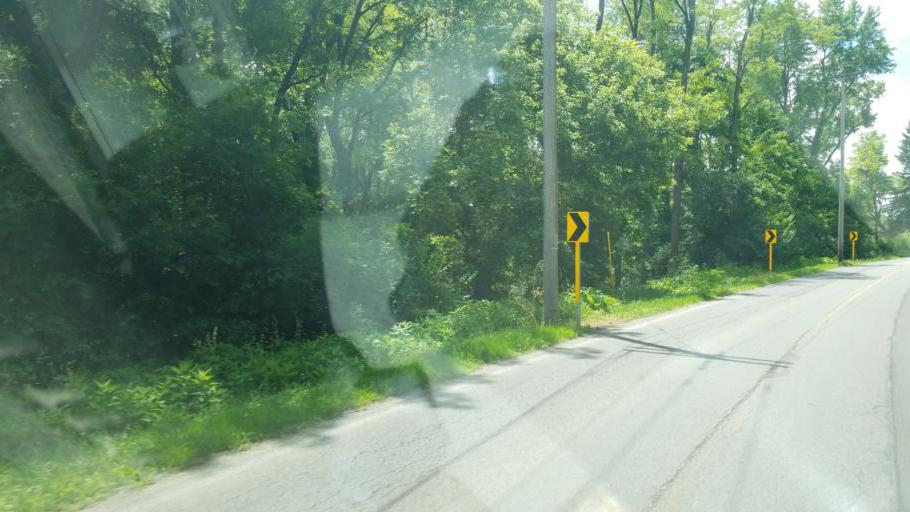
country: US
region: Ohio
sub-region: Richland County
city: Ontario
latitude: 40.7279
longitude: -82.5707
